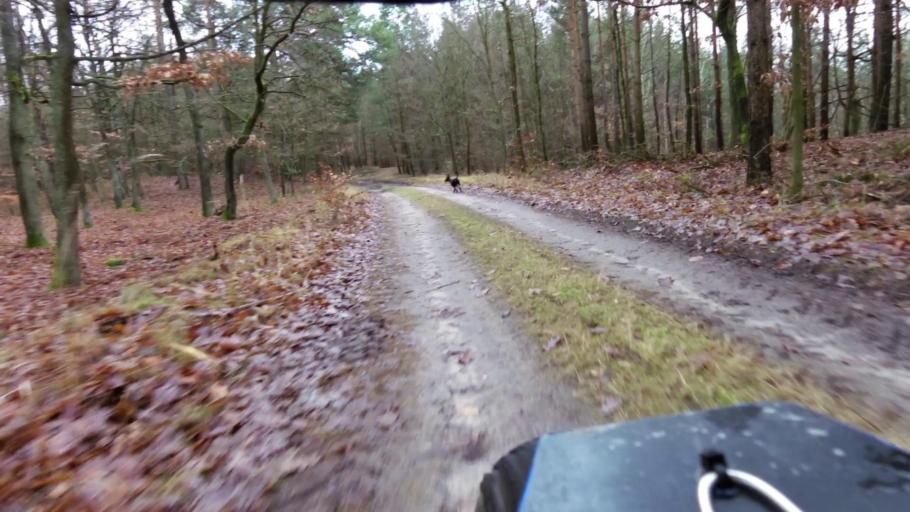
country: PL
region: Lubusz
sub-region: Powiat gorzowski
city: Bogdaniec
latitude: 52.6926
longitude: 15.0372
